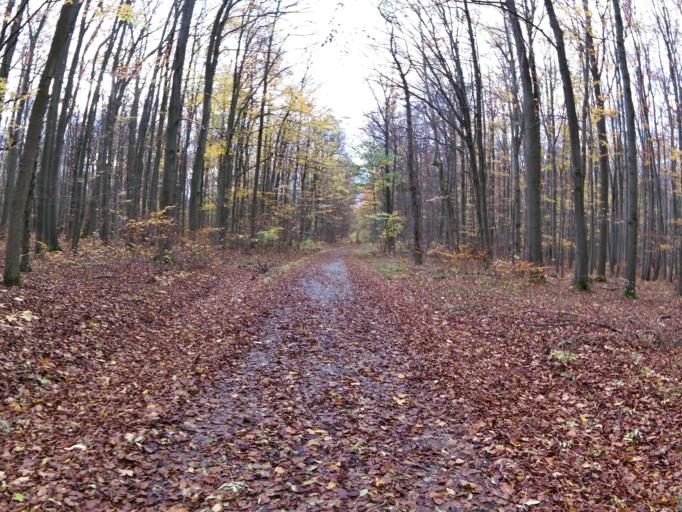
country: DE
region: Thuringia
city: Bischofroda
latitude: 51.0799
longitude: 10.3996
